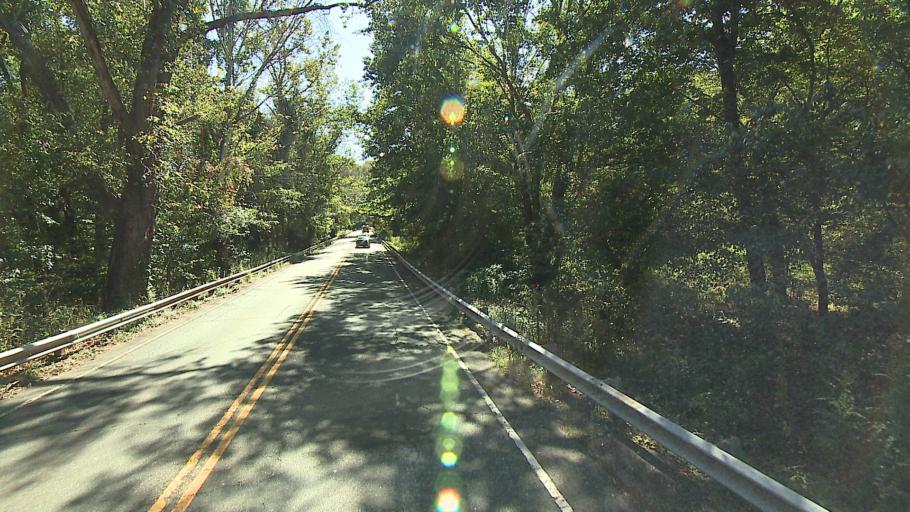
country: US
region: Connecticut
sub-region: New Haven County
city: Orange
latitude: 41.2855
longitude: -73.0409
